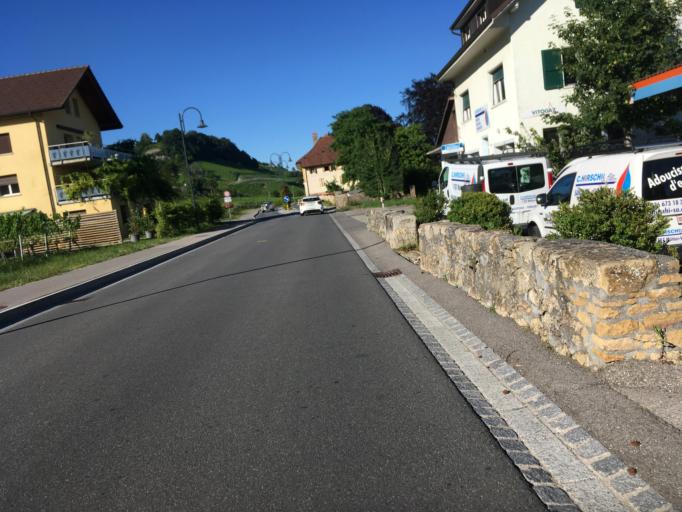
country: CH
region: Fribourg
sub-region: See District
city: Bas-Vully
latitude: 46.9512
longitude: 7.0914
